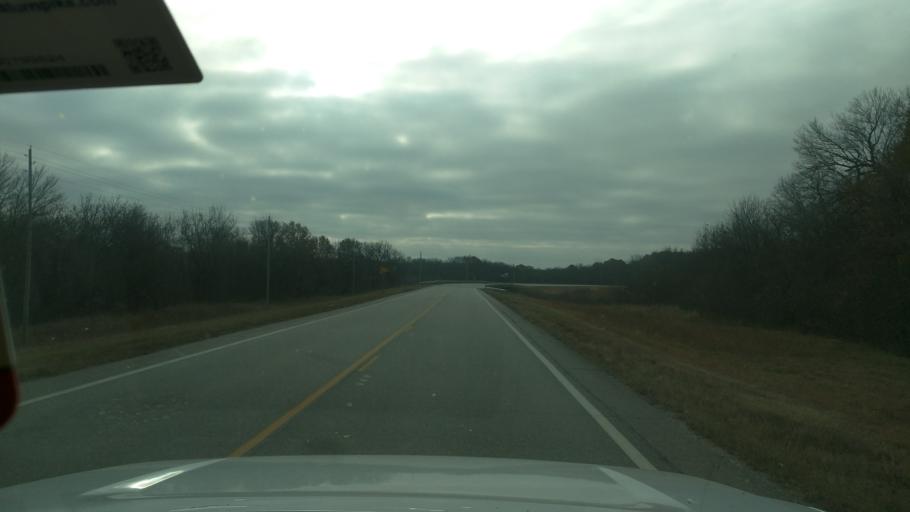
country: US
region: Kansas
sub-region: Greenwood County
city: Eureka
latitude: 37.7102
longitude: -96.2252
